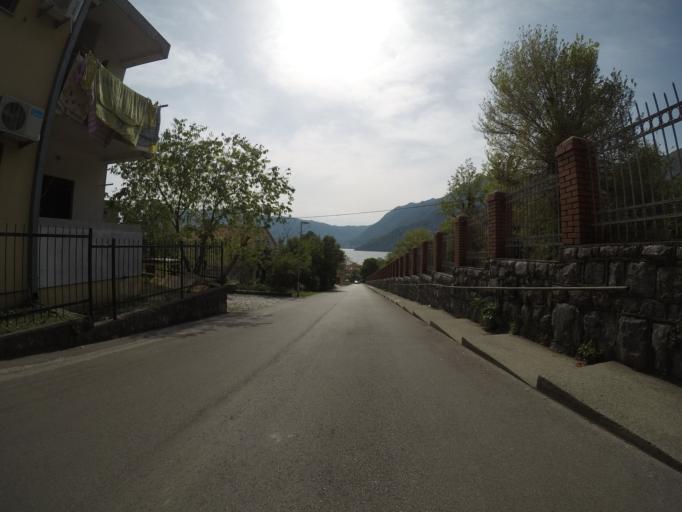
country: ME
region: Kotor
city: Risan
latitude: 42.5135
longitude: 18.6984
